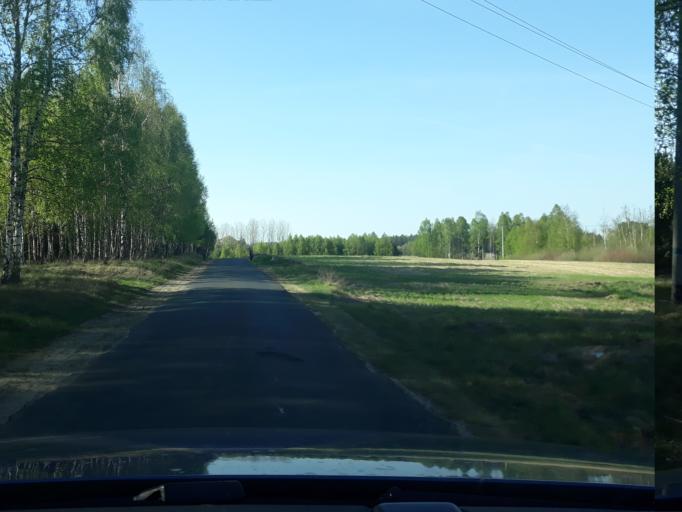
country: PL
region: Pomeranian Voivodeship
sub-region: Powiat czluchowski
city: Przechlewo
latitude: 53.8671
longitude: 17.3342
